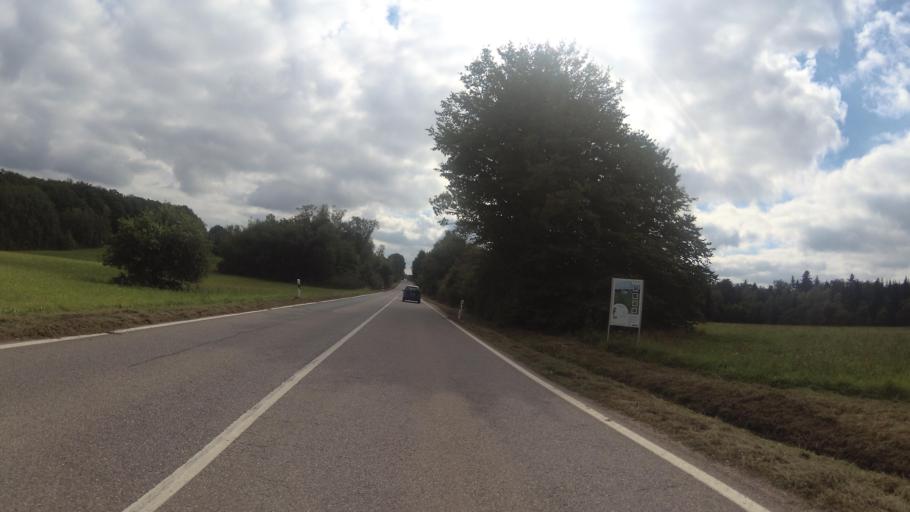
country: DE
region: Saarland
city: Grossrosseln
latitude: 49.2046
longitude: 6.8097
